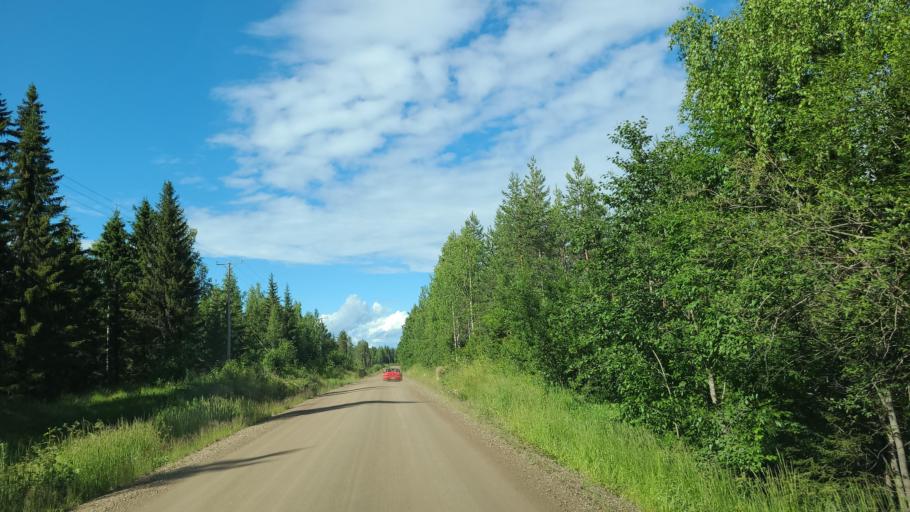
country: FI
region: Northern Savo
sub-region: Koillis-Savo
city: Kaavi
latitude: 62.9377
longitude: 28.7632
